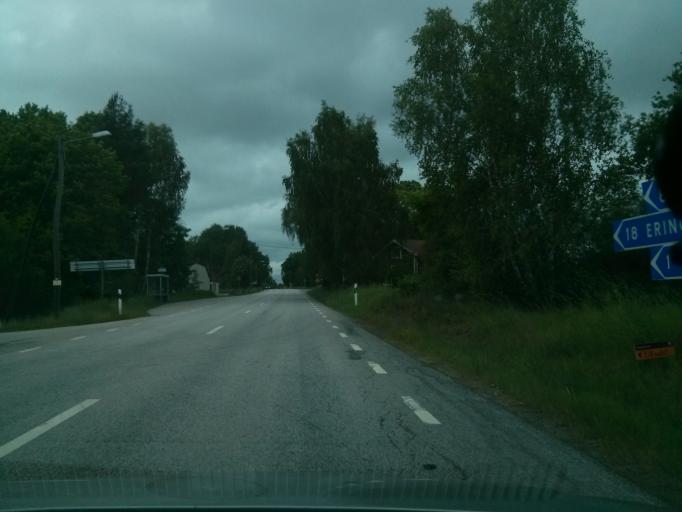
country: SE
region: Blekinge
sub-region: Karlskrona Kommun
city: Nattraby
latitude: 56.2957
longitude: 15.4841
